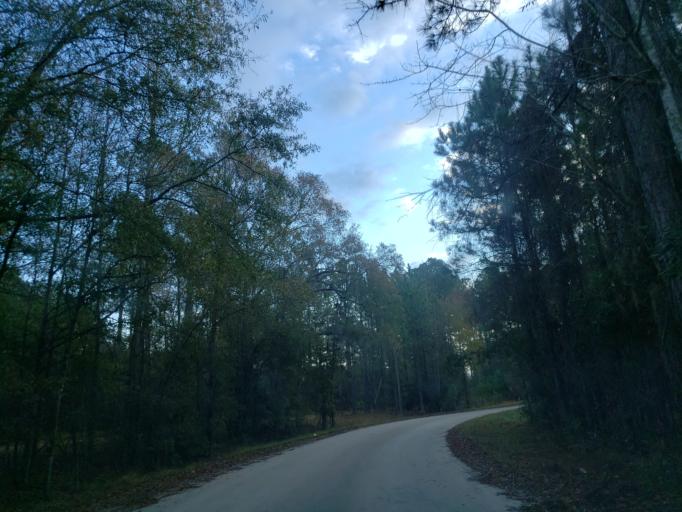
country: US
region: Georgia
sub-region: Chatham County
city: Bloomingdale
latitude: 32.1192
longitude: -81.3387
